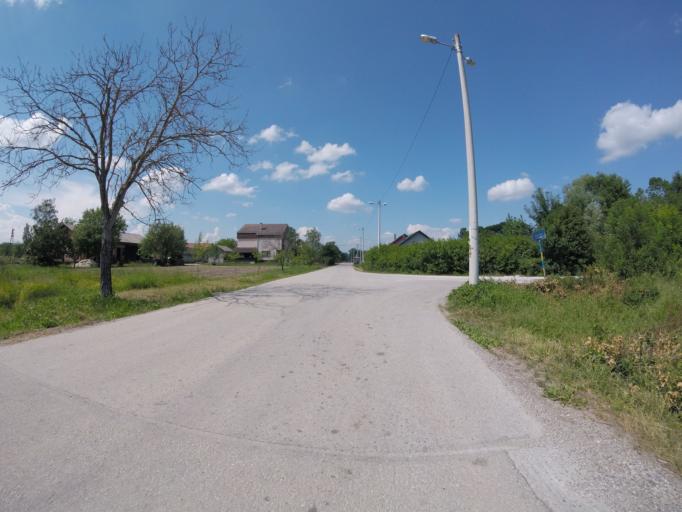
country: HR
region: Zagrebacka
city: Kuce
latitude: 45.6734
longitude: 16.1833
